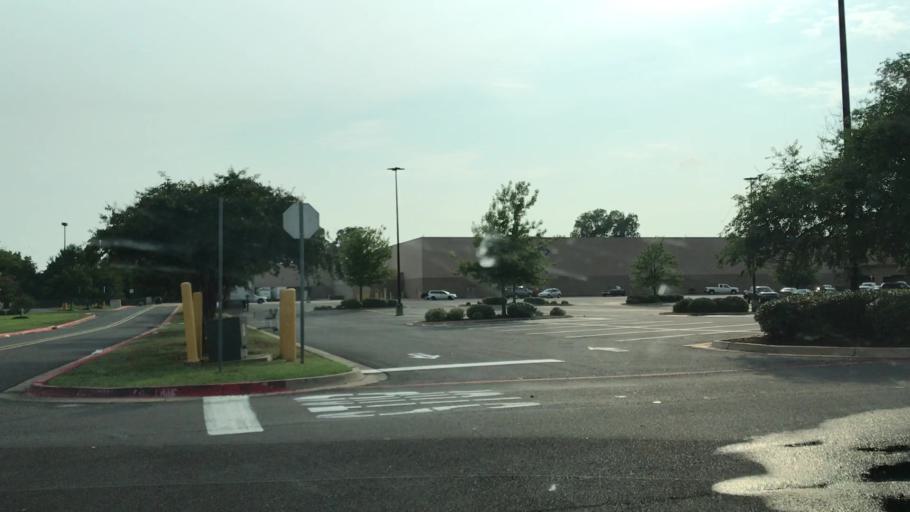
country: US
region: Louisiana
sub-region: Bossier Parish
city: Bossier City
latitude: 32.4378
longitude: -93.7171
